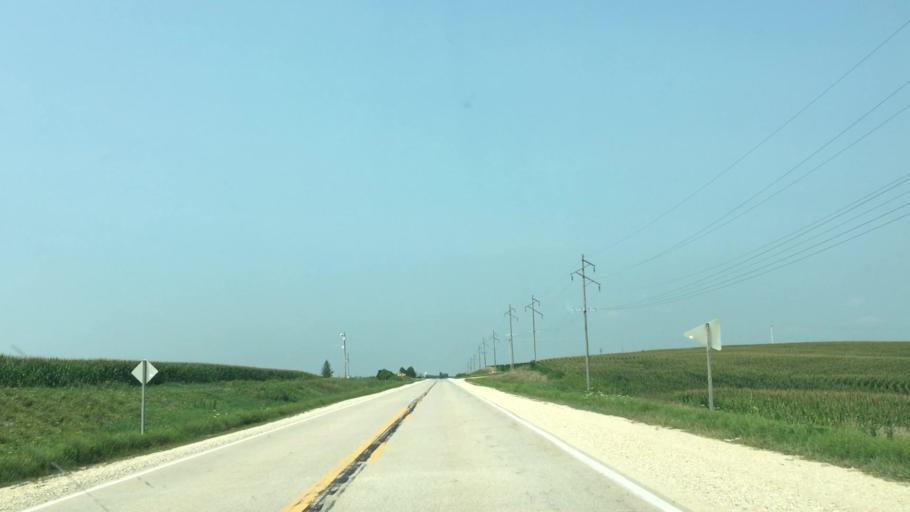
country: US
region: Iowa
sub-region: Winneshiek County
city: Decorah
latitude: 43.1452
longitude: -91.8642
